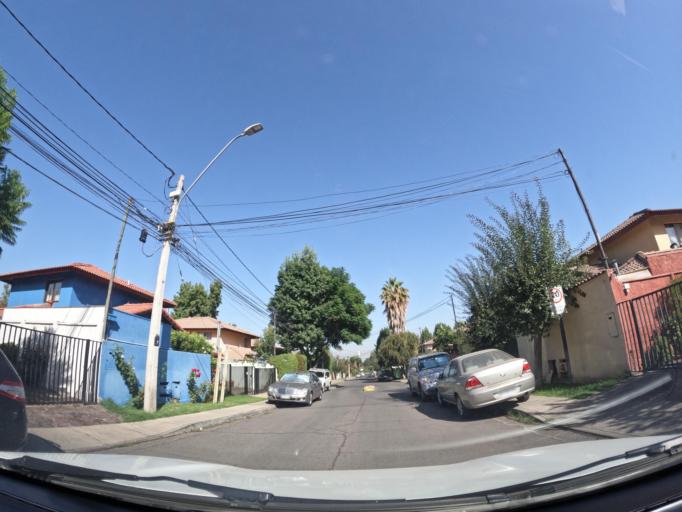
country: CL
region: Santiago Metropolitan
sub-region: Provincia de Santiago
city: Villa Presidente Frei, Nunoa, Santiago, Chile
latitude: -33.5051
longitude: -70.5578
